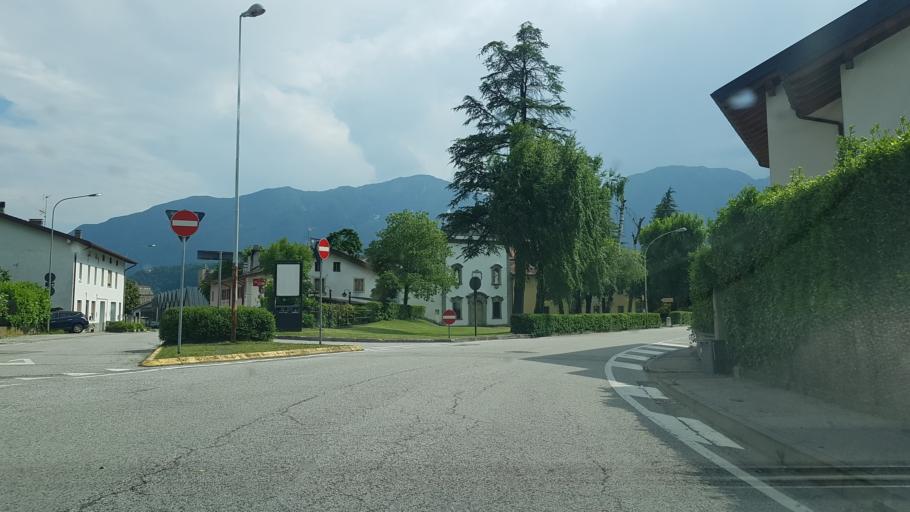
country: IT
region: Friuli Venezia Giulia
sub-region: Provincia di Udine
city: Tolmezzo
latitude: 46.3999
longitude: 13.0180
